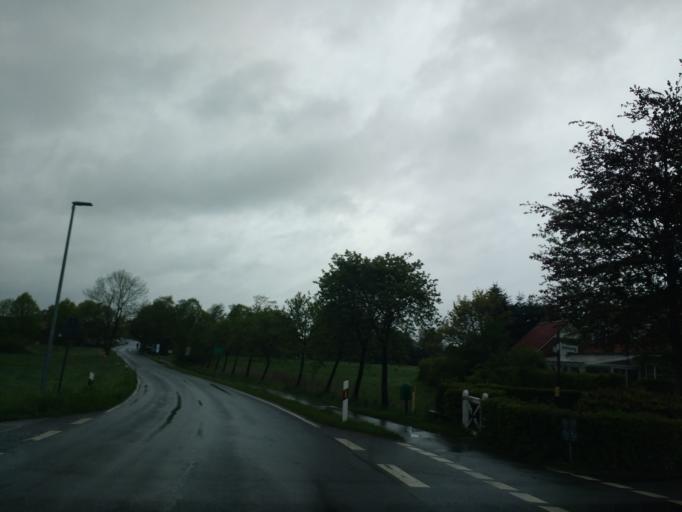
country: DE
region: Schleswig-Holstein
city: Waabs
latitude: 54.5504
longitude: 9.9927
